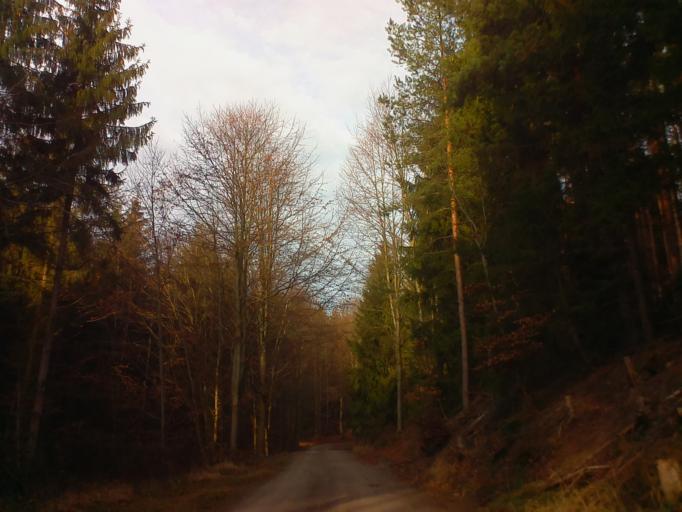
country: DE
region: Thuringia
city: Hummelshain
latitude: 50.7570
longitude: 11.6451
